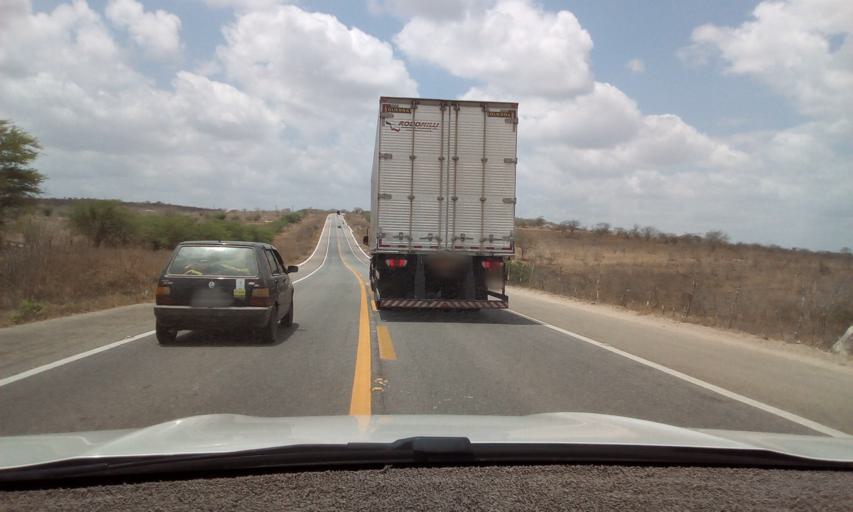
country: BR
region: Pernambuco
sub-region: Taquaritinga Do Norte
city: Taquaritinga do Norte
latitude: -7.7228
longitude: -36.0740
